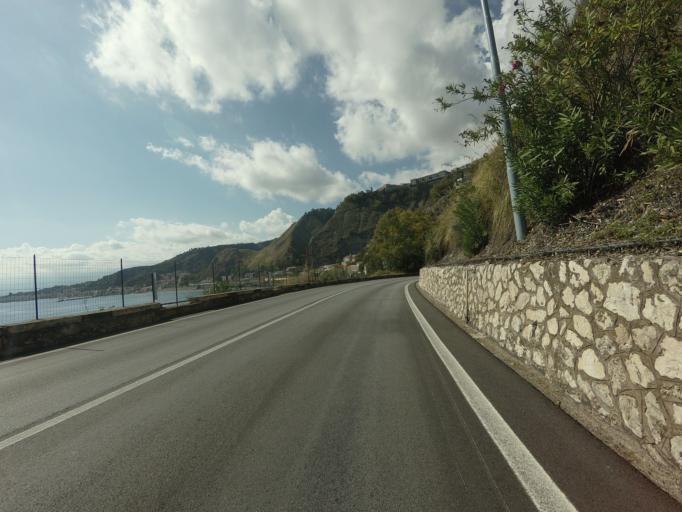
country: IT
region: Sicily
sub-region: Messina
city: Taormina
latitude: 37.8478
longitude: 15.2914
